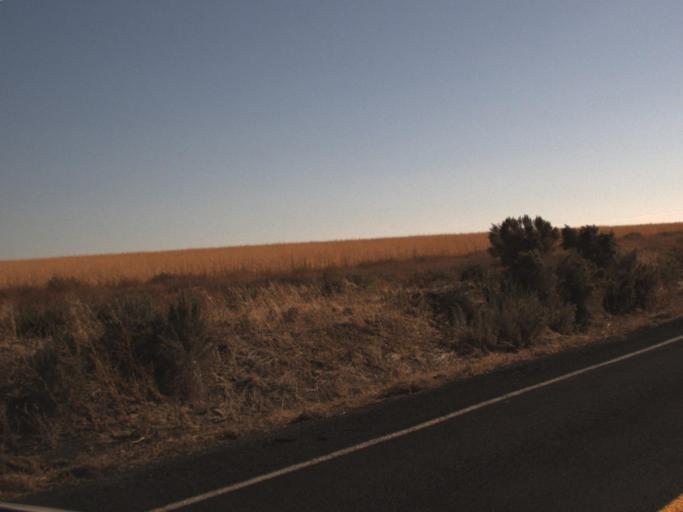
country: US
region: Washington
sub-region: Adams County
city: Ritzville
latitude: 47.0087
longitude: -118.6637
